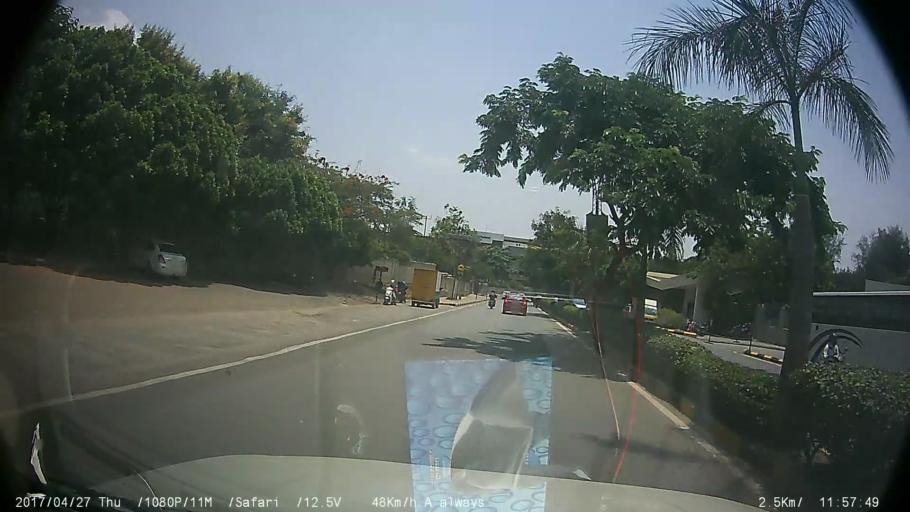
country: IN
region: Karnataka
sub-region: Bangalore Urban
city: Bangalore
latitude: 12.8525
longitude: 77.6604
